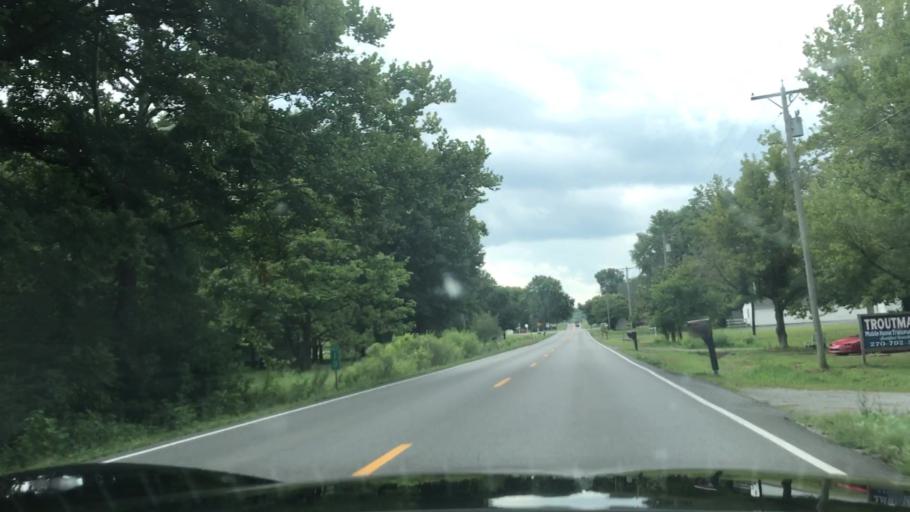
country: US
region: Kentucky
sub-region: Muhlenberg County
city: Central City
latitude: 37.1997
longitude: -87.0369
